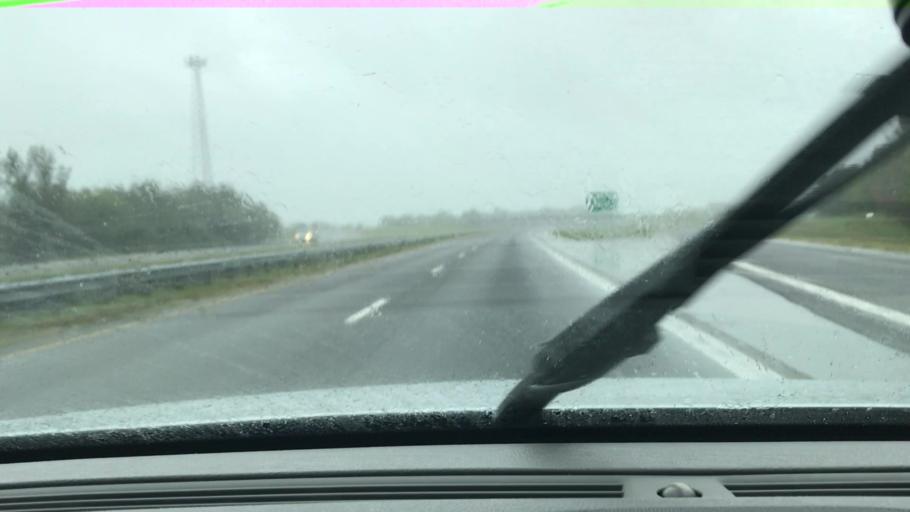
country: US
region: Alabama
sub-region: Limestone County
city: Ardmore
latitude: 34.9693
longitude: -86.8851
